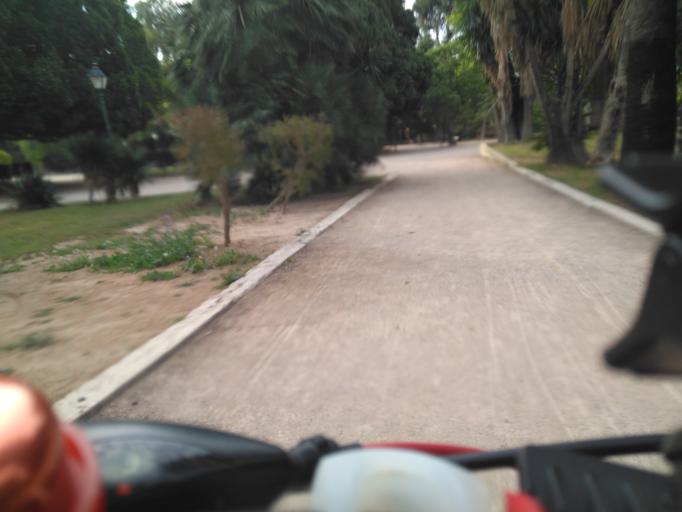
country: ES
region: Valencia
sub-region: Provincia de Valencia
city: Valencia
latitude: 39.4820
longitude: -0.3680
